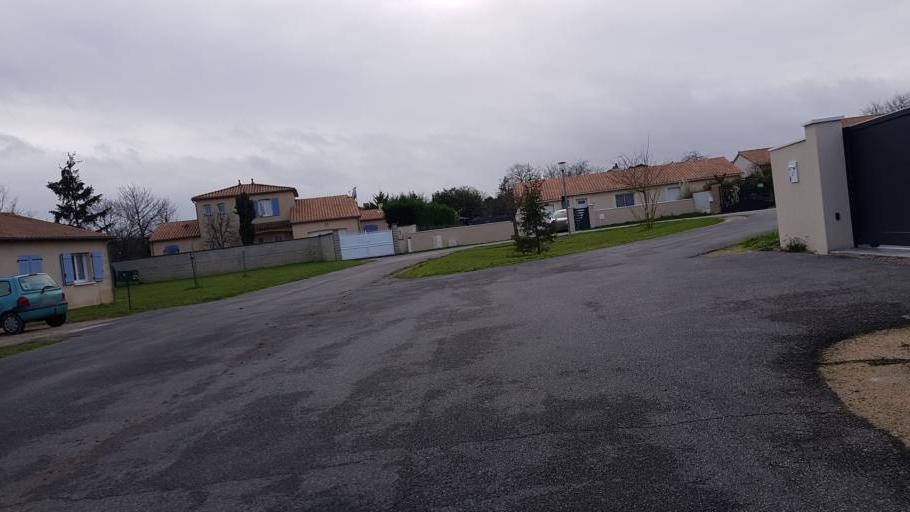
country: FR
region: Poitou-Charentes
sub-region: Departement de la Vienne
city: Avanton
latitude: 46.6639
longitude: 0.3131
